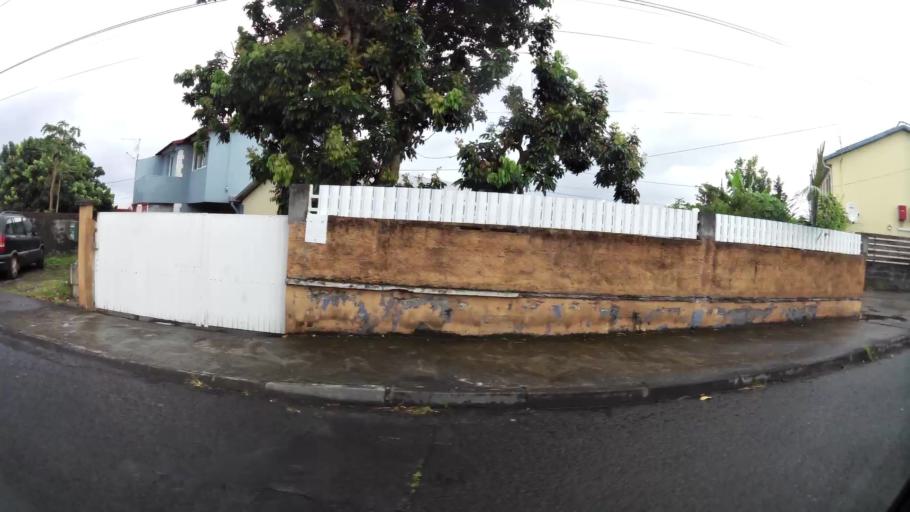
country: RE
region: Reunion
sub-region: Reunion
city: Saint-Andre
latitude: -20.9356
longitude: 55.6488
